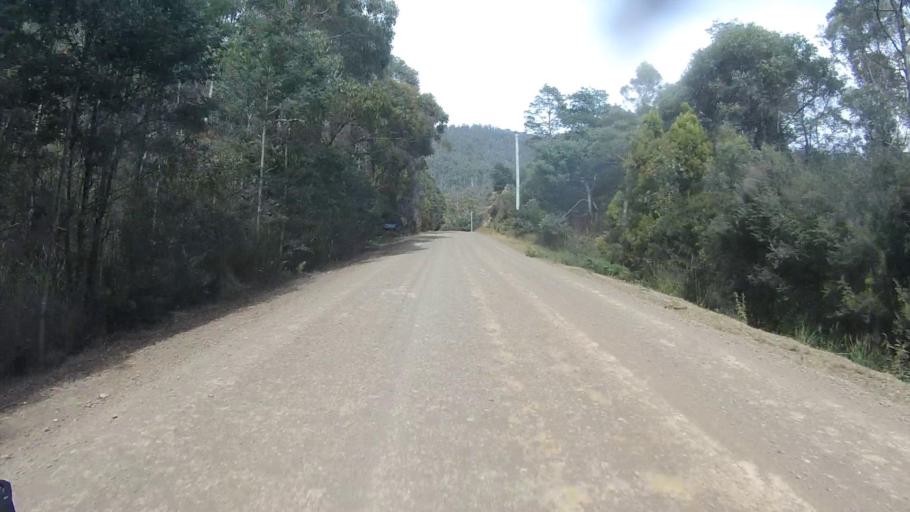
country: AU
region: Tasmania
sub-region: Sorell
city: Sorell
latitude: -42.6891
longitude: 147.8685
